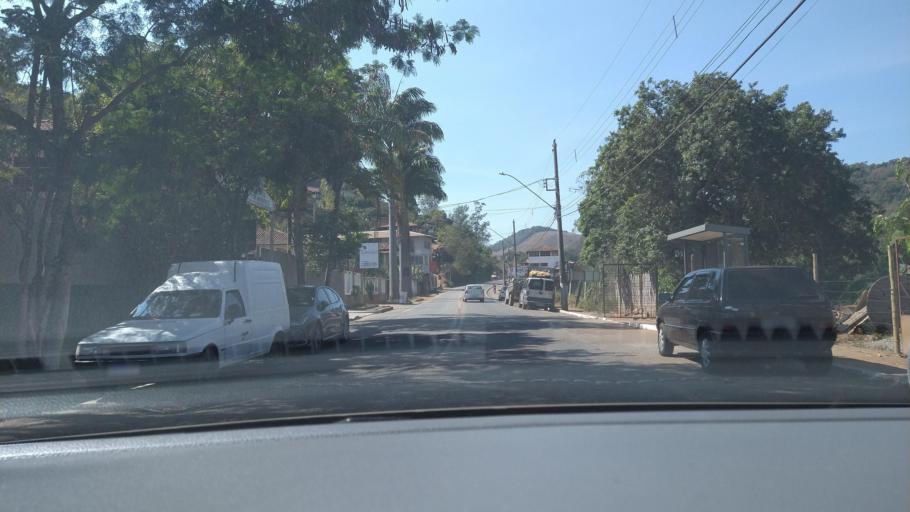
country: BR
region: Minas Gerais
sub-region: Rio Piracicaba
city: Rio Piracicaba
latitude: -19.9274
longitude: -43.1676
